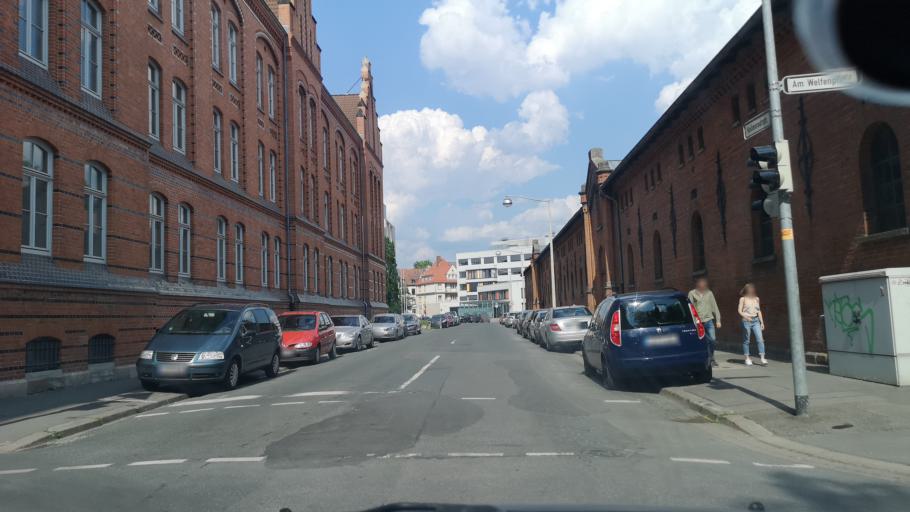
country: DE
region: Lower Saxony
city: Hannover
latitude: 52.3863
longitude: 9.7425
